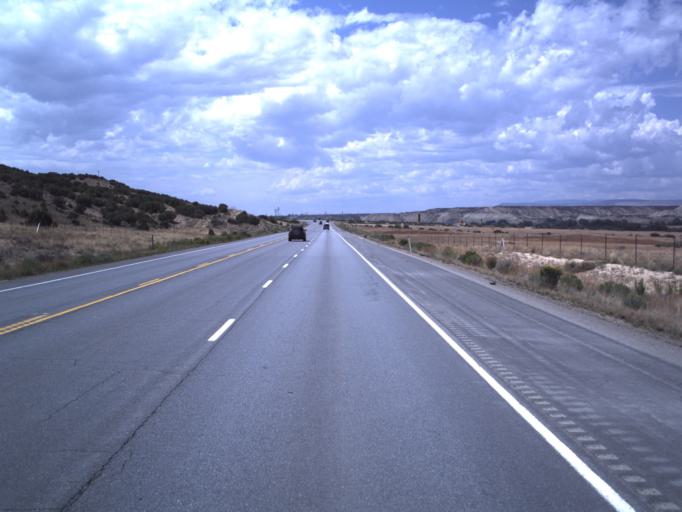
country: US
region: Utah
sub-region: Duchesne County
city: Duchesne
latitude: 40.1703
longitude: -110.3240
